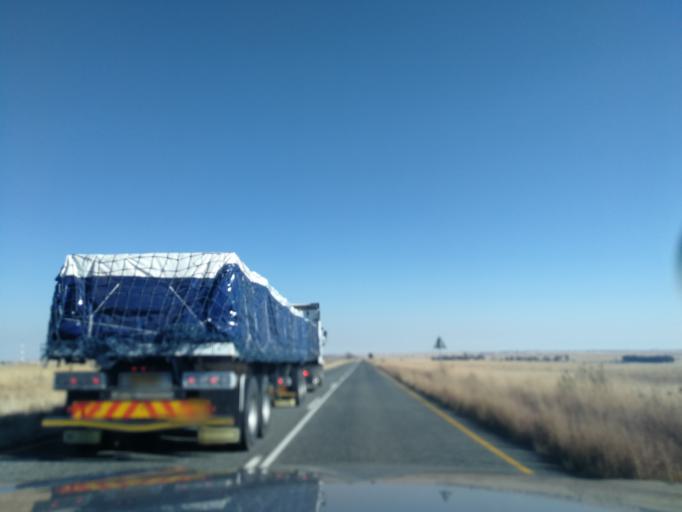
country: ZA
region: Orange Free State
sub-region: Thabo Mofutsanyana District Municipality
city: Senekal
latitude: -27.9519
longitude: 27.5914
